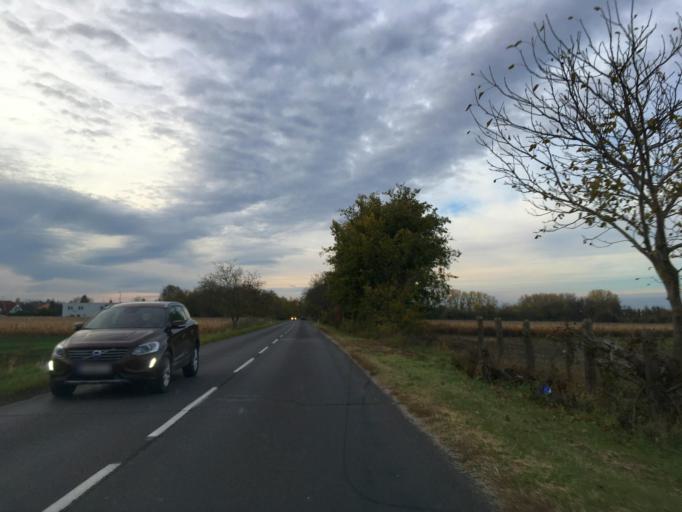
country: SK
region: Trnavsky
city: Dunajska Streda
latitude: 48.0094
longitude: 17.5882
